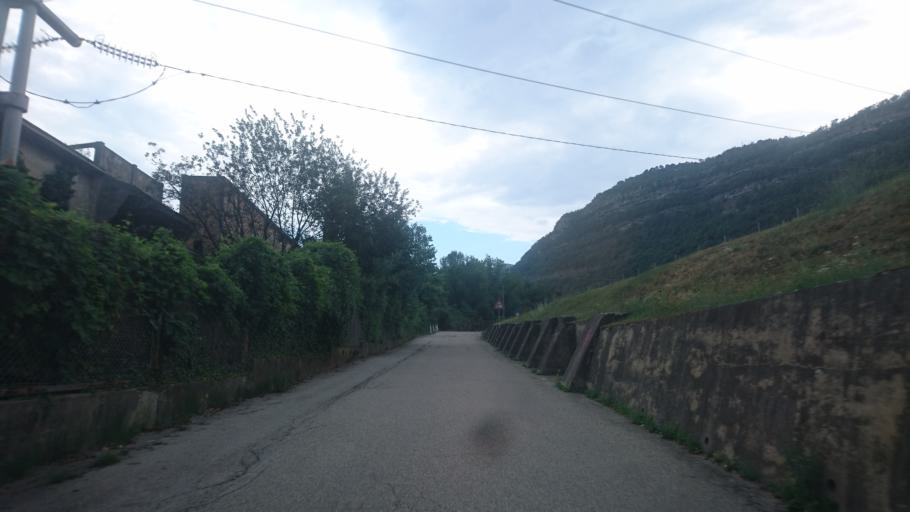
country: IT
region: Trentino-Alto Adige
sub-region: Provincia di Trento
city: Marco
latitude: 45.8385
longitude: 10.9998
